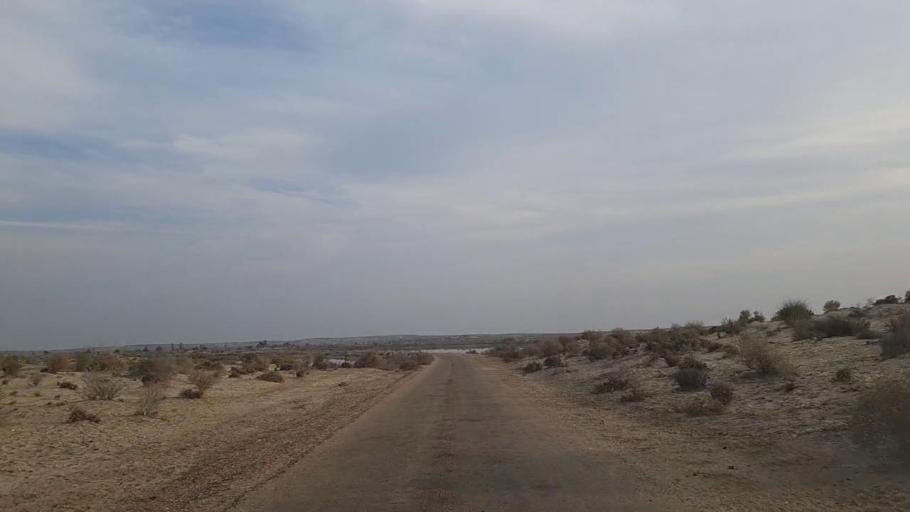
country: PK
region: Sindh
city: Daur
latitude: 26.4996
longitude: 68.5213
